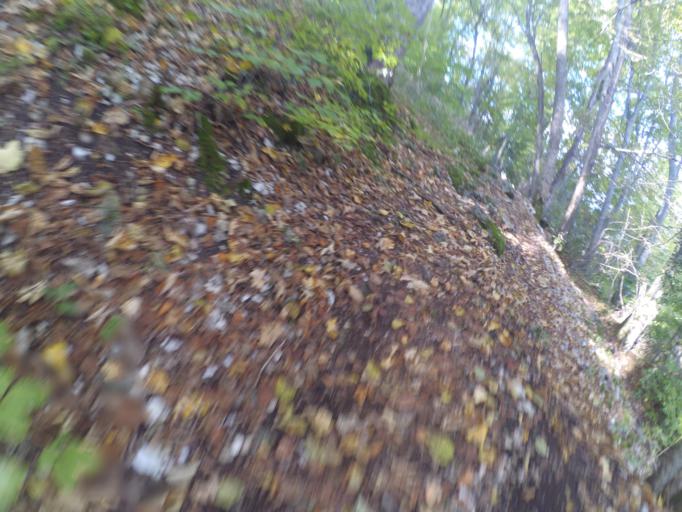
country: DE
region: Baden-Wuerttemberg
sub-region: Regierungsbezirk Stuttgart
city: Heubach
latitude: 48.7832
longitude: 9.9236
